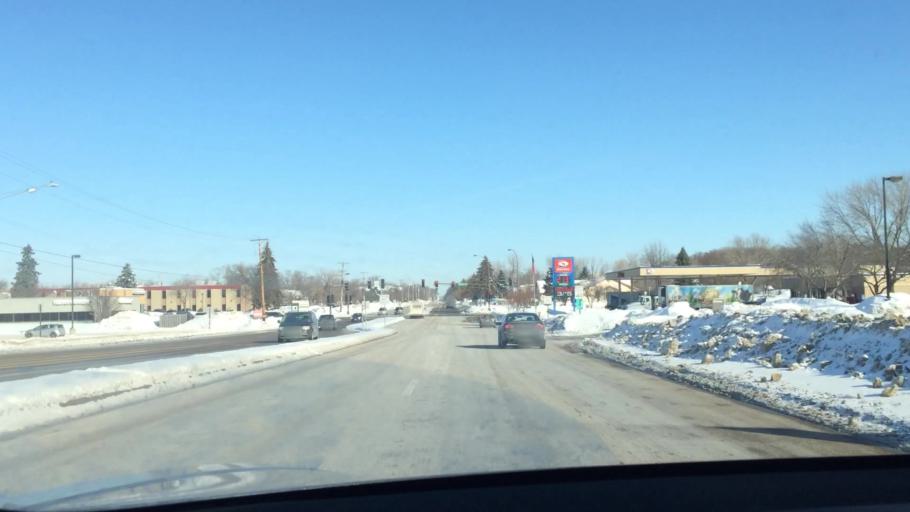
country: US
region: Minnesota
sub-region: Hennepin County
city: Plymouth
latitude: 45.0127
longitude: -93.4615
